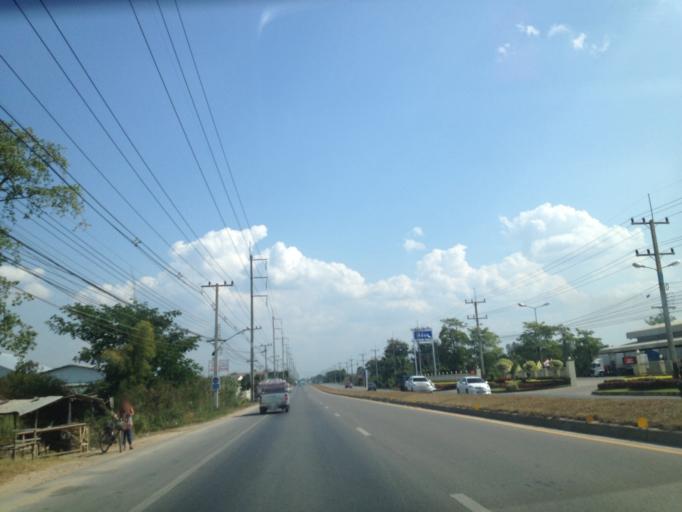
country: TH
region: Lamphun
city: Wiang Nong Long
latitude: 18.4517
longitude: 98.7340
